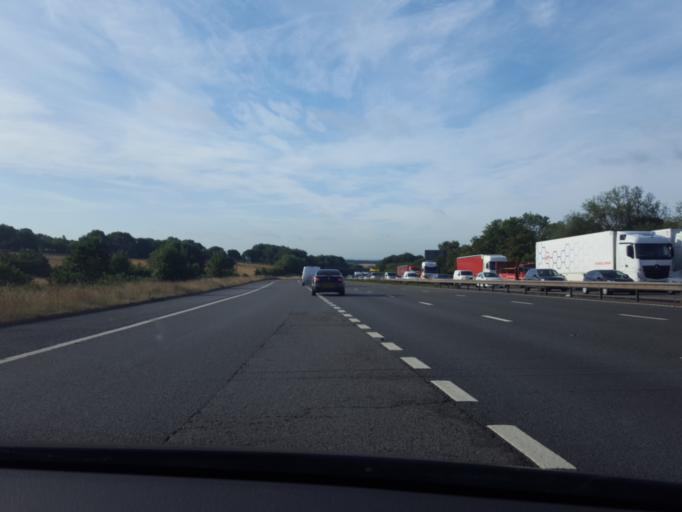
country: GB
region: England
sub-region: Leicestershire
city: Markfield
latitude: 52.6924
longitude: -1.2910
